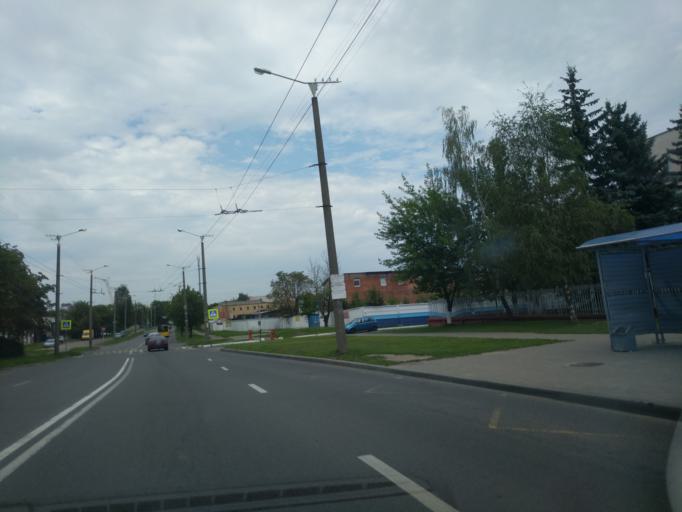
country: BY
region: Minsk
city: Novoye Medvezhino
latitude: 53.8860
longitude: 27.4810
